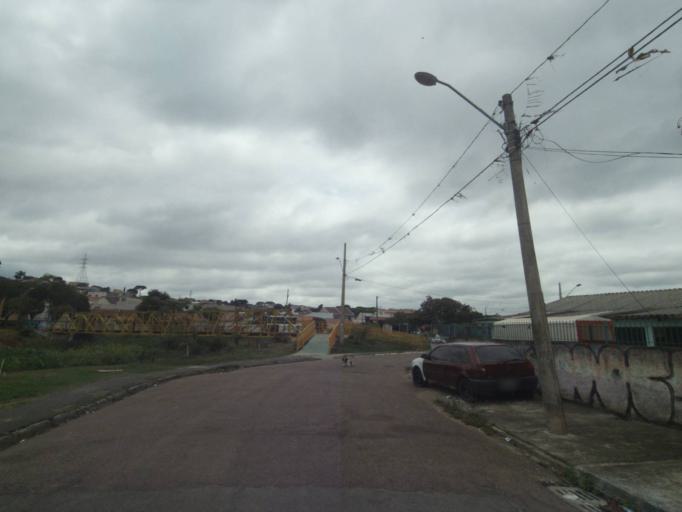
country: BR
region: Parana
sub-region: Sao Jose Dos Pinhais
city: Sao Jose dos Pinhais
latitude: -25.5327
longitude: -49.2550
